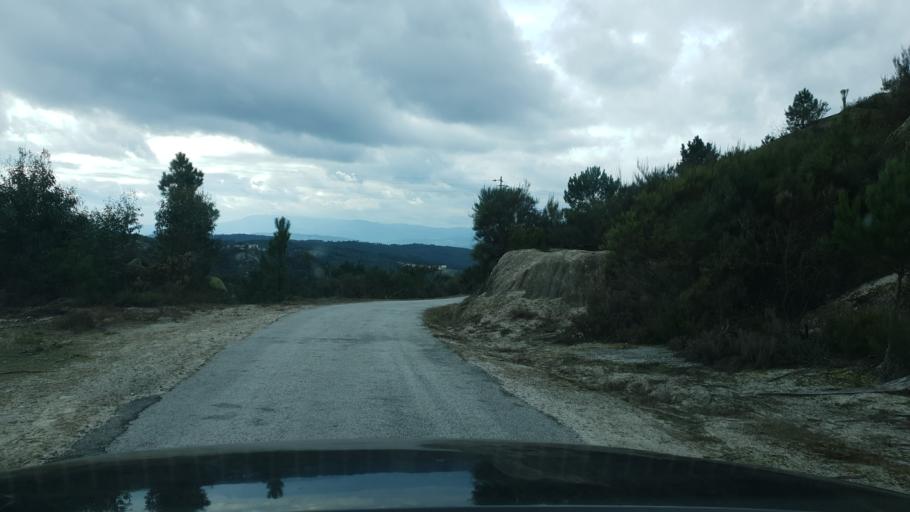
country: PT
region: Viseu
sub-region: Castro Daire
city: Castro Daire
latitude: 40.8722
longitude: -7.9877
